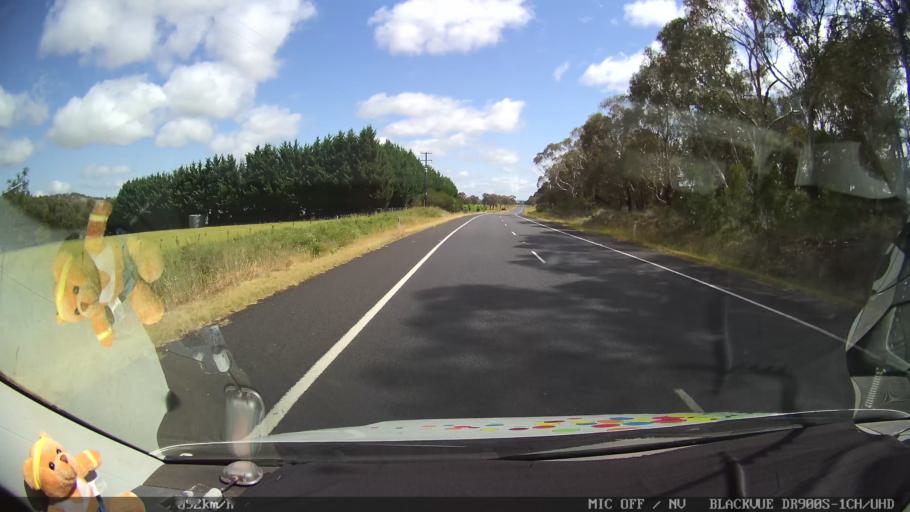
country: AU
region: New South Wales
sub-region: Glen Innes Severn
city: Glen Innes
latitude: -29.8776
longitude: 151.7342
